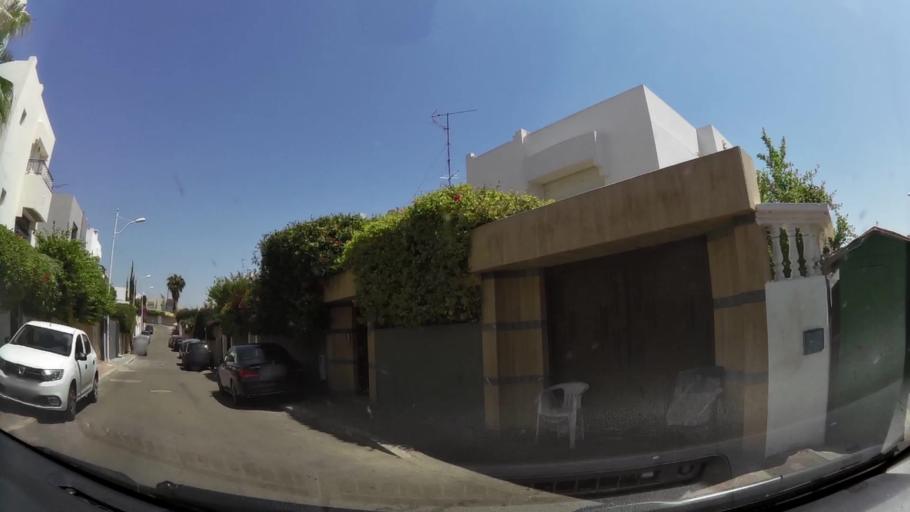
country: MA
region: Souss-Massa-Draa
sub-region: Agadir-Ida-ou-Tnan
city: Agadir
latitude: 30.4327
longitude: -9.5858
